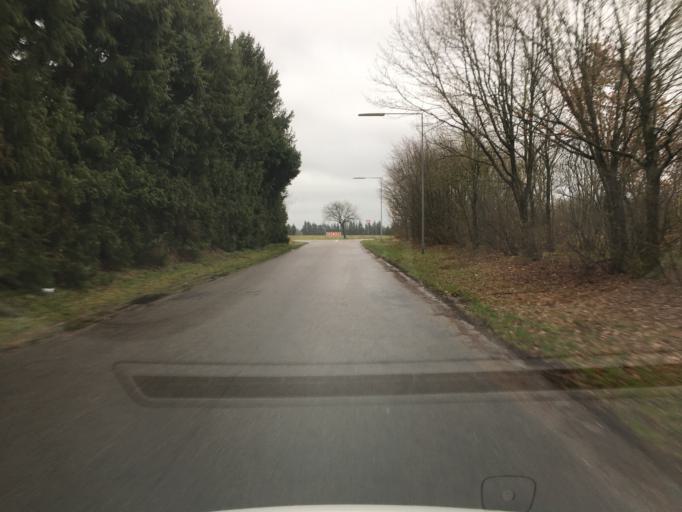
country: DK
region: South Denmark
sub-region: Aabenraa Kommune
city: Tinglev
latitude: 54.9265
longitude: 9.2304
